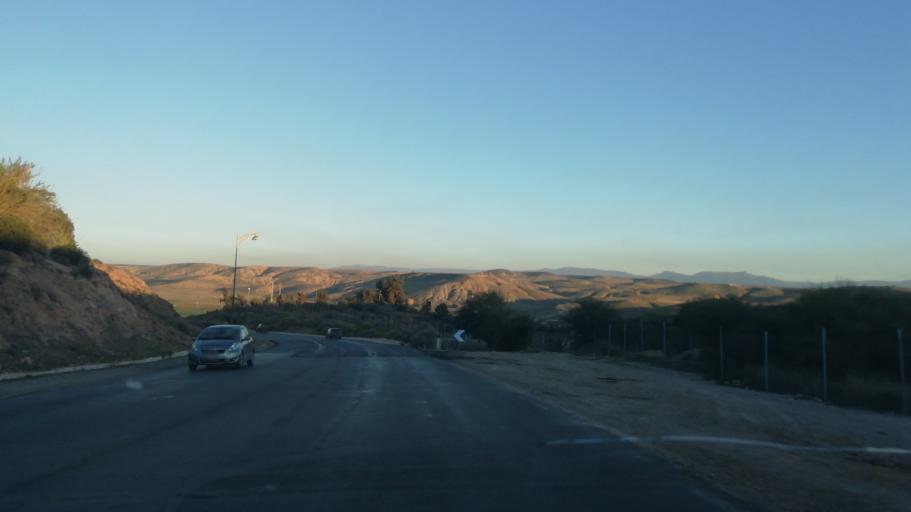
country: DZ
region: Tlemcen
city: Nedroma
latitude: 34.8879
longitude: -1.6496
